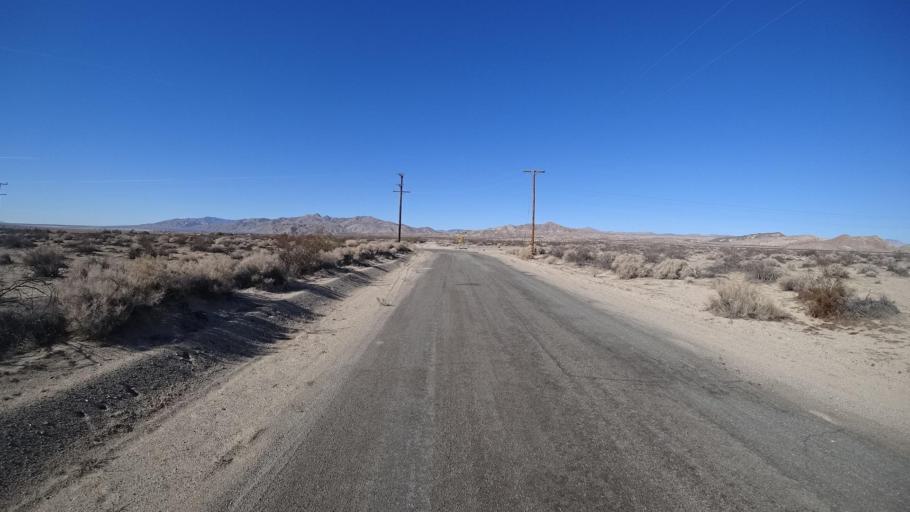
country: US
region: California
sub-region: Kern County
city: California City
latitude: 35.3162
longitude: -117.9498
